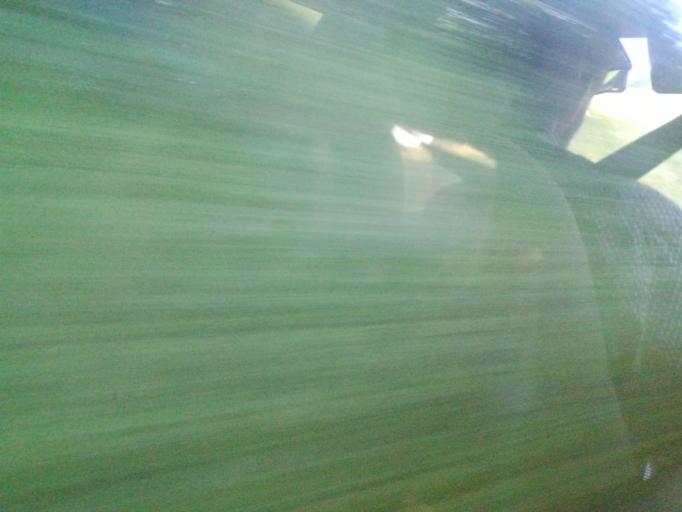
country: IE
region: Leinster
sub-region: Kilkenny
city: Castlecomer
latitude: 52.7437
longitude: -7.2356
